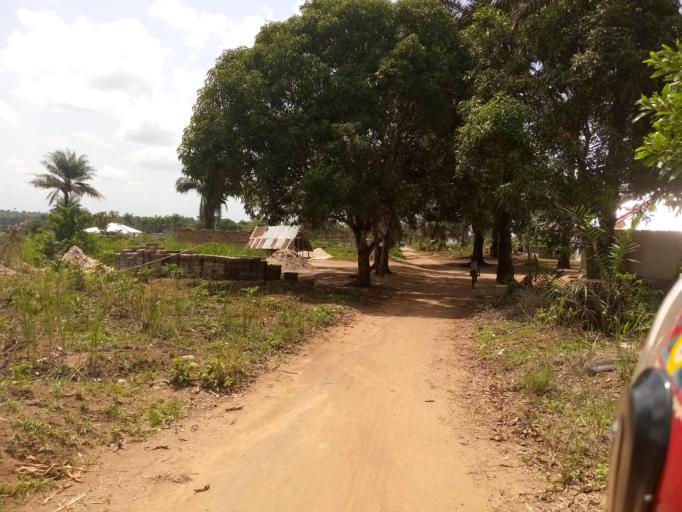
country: SL
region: Western Area
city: Waterloo
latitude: 8.3558
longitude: -13.0089
